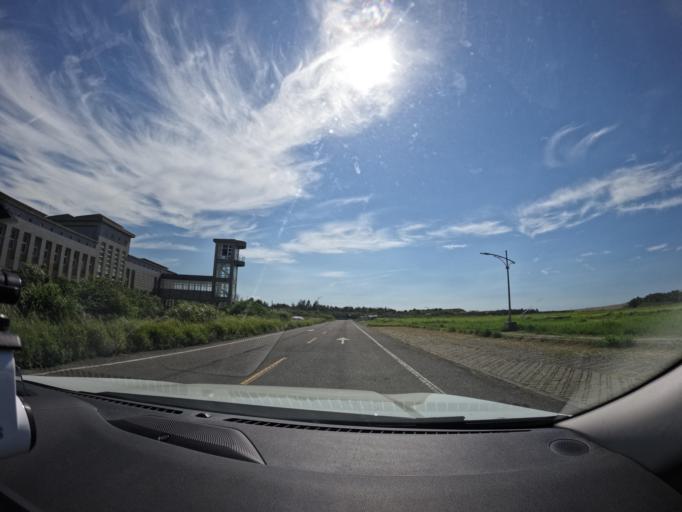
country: TW
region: Taiwan
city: Taoyuan City
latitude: 25.1132
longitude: 121.2402
